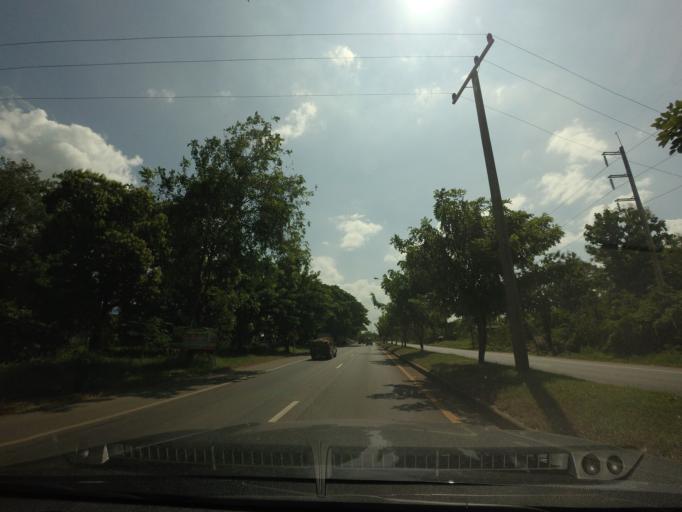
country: TH
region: Phetchabun
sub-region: Amphoe Bueng Sam Phan
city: Bueng Sam Phan
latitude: 15.8725
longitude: 101.0143
